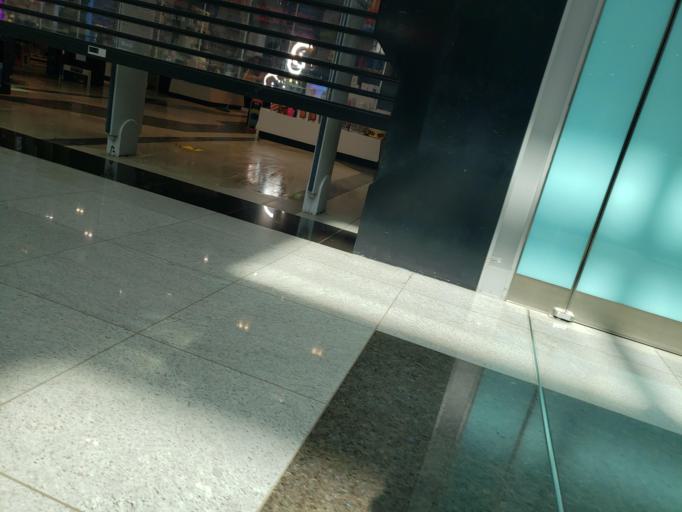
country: AE
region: Dubai
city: Dubai
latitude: 25.1970
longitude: 55.2777
